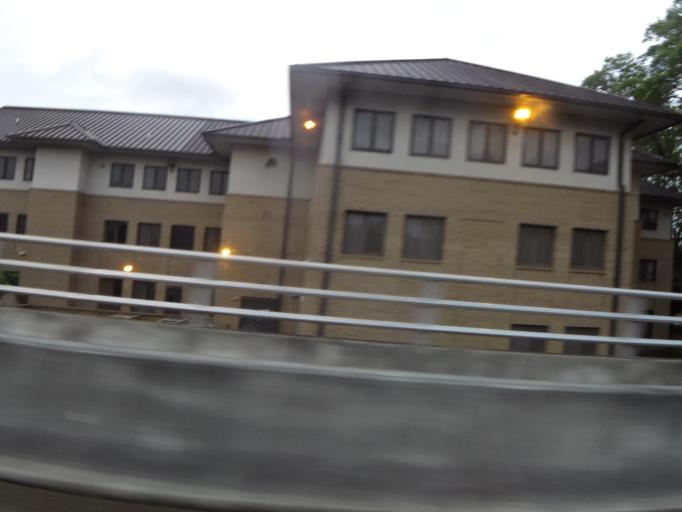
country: US
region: Florida
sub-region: Duval County
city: Jacksonville
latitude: 30.3269
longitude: -81.6473
